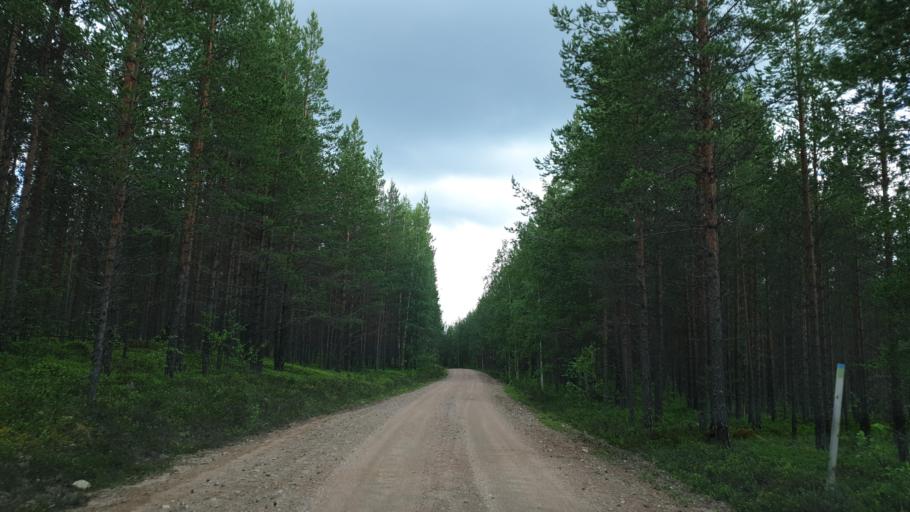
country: SE
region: Jaemtland
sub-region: Harjedalens Kommun
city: Sveg
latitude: 62.0384
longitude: 14.4956
